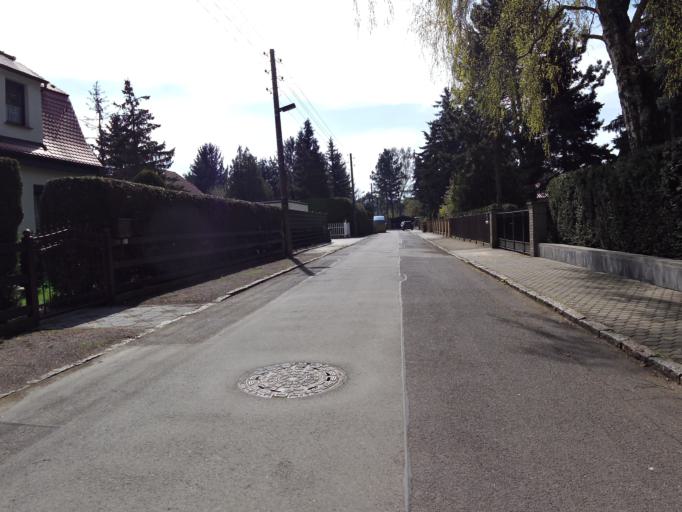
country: DE
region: Saxony
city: Markranstadt
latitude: 51.3138
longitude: 12.2714
